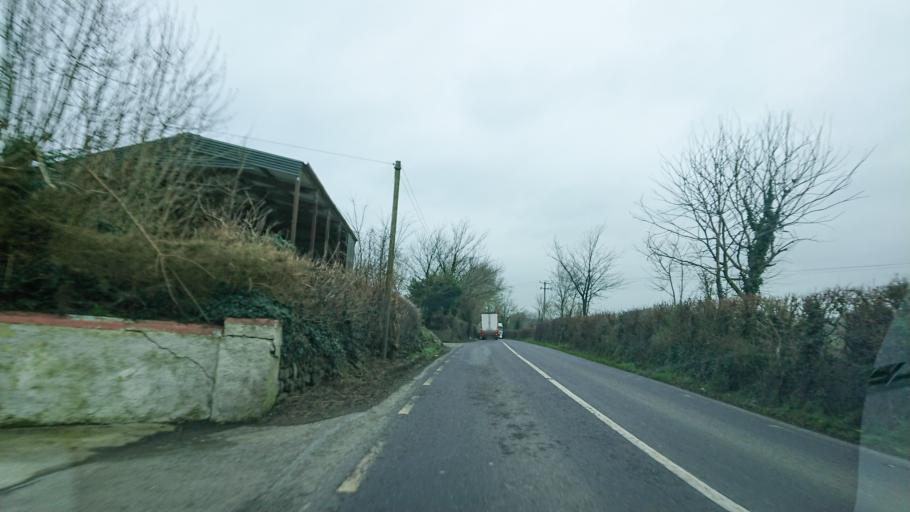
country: IE
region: Munster
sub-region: County Cork
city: Bandon
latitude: 51.7449
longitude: -8.8220
